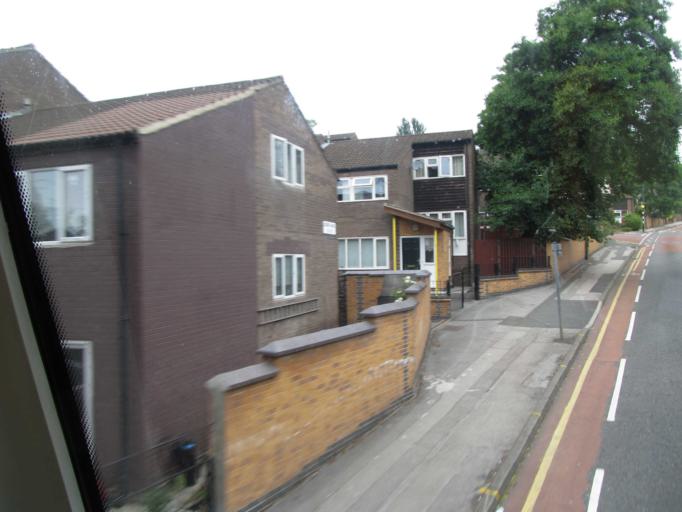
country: GB
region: England
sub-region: Nottingham
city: Nottingham
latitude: 52.9641
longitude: -1.1450
